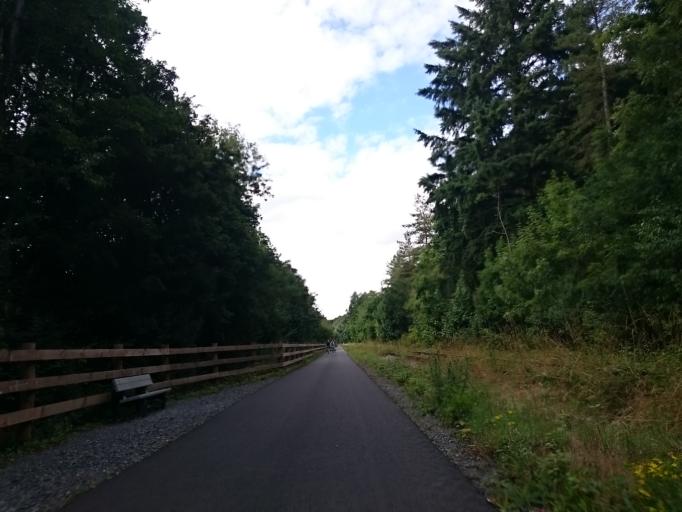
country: FR
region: Lower Normandy
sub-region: Departement du Calvados
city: Thury-Harcourt
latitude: 49.0220
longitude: -0.4652
